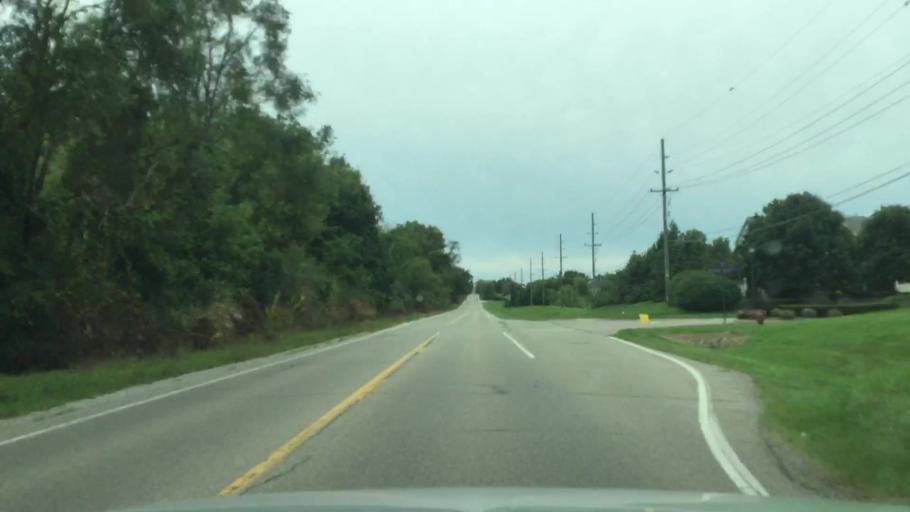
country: US
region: Michigan
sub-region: Washtenaw County
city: Ypsilanti
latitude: 42.2156
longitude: -83.6601
